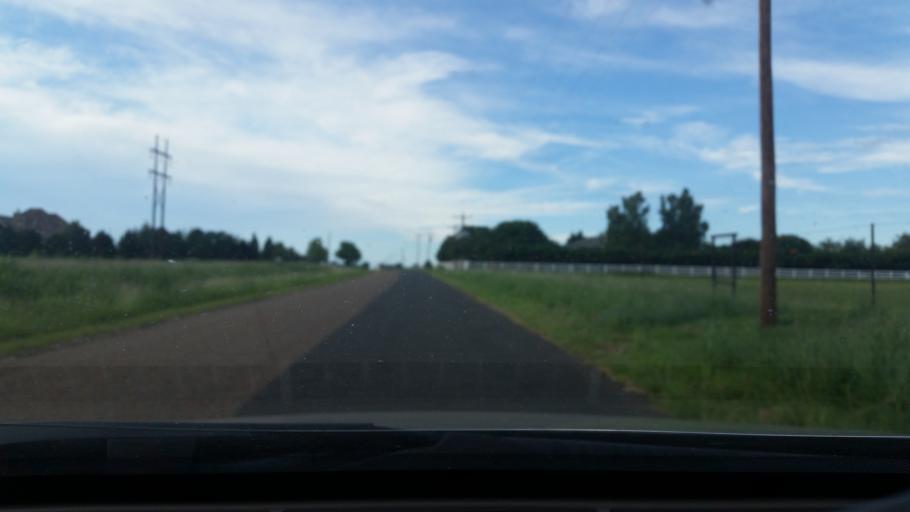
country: US
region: New Mexico
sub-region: Curry County
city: Clovis
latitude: 34.4547
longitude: -103.1784
